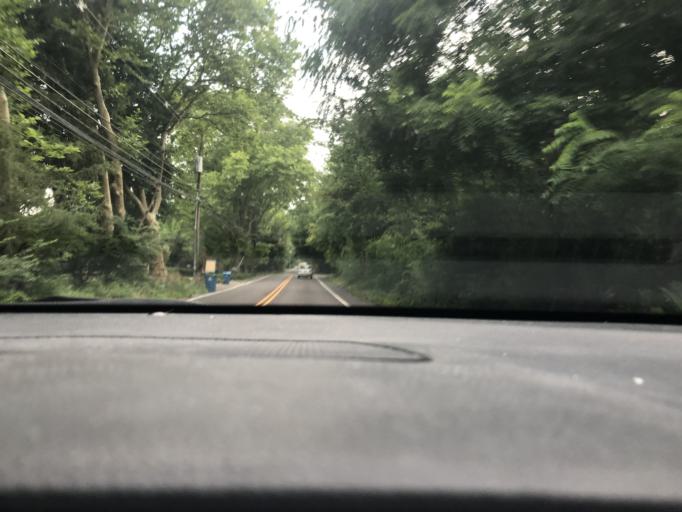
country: US
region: Pennsylvania
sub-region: Montgomery County
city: Spring House
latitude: 40.1758
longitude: -75.2373
